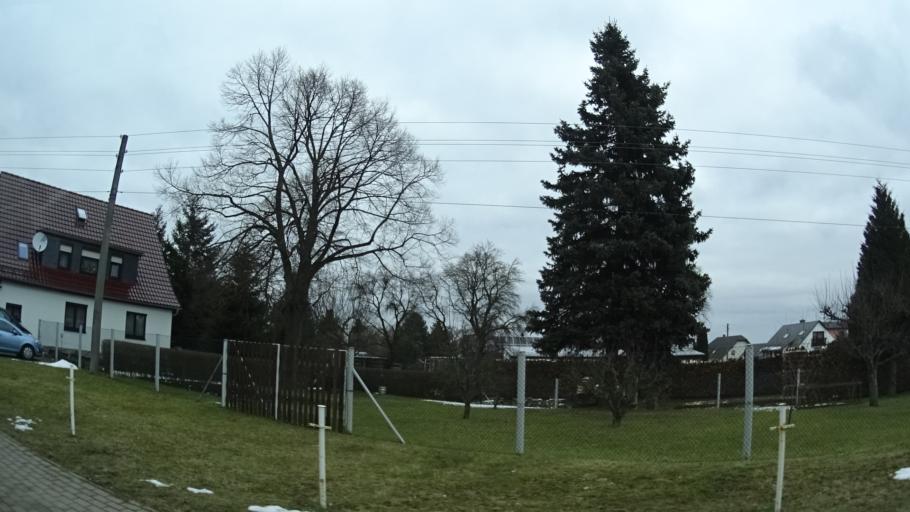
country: DE
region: Thuringia
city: Pennewitz
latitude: 50.6586
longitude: 11.0497
